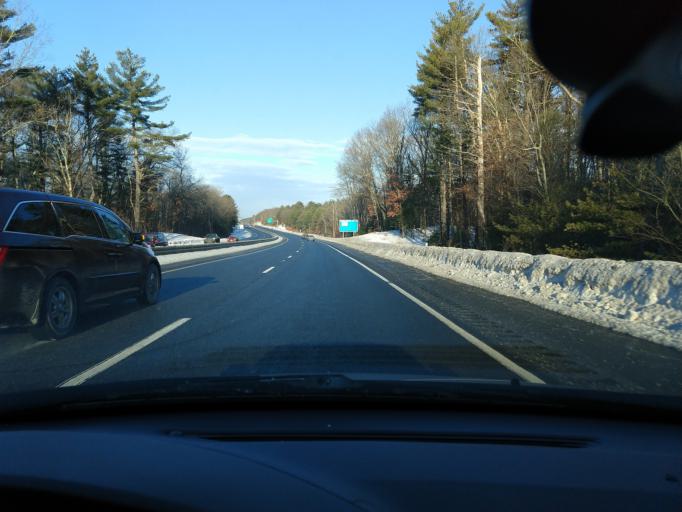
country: US
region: Massachusetts
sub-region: Middlesex County
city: Acton
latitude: 42.4927
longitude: -71.4617
